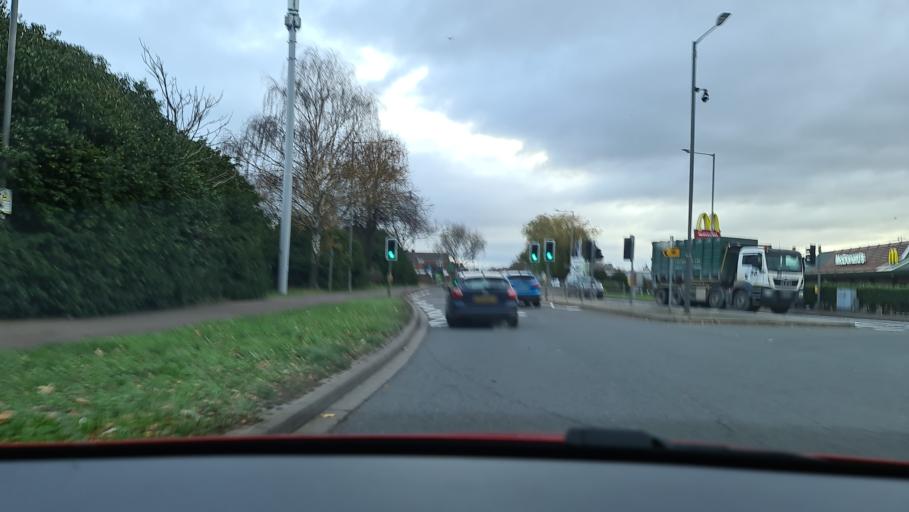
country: GB
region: England
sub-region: Buckinghamshire
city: Aylesbury
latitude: 51.8248
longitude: -0.8341
